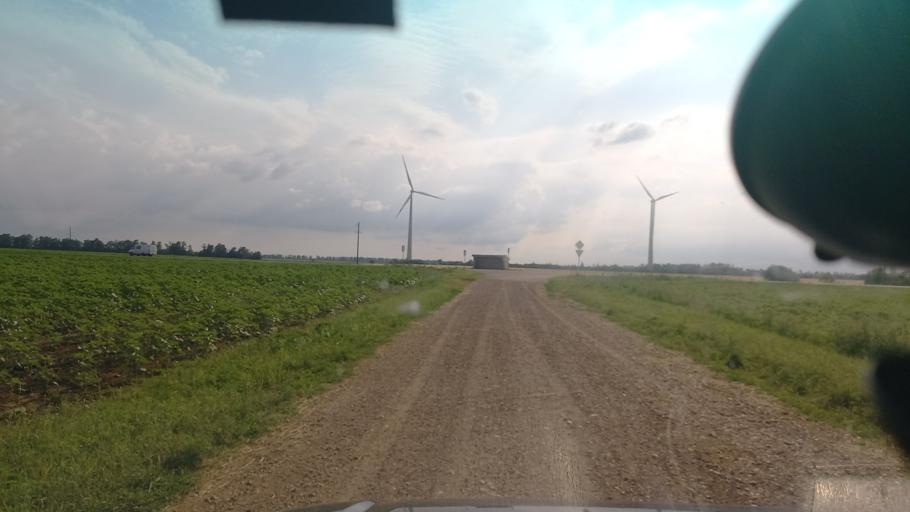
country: RU
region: Adygeya
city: Giaginskaya
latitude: 44.9520
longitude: 40.0850
